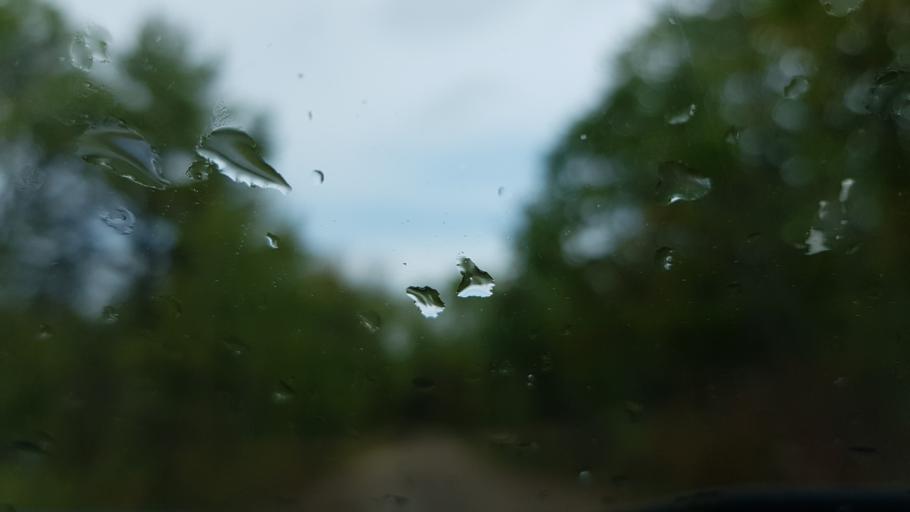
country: CA
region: Ontario
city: Gravenhurst
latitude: 44.6974
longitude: -79.0012
